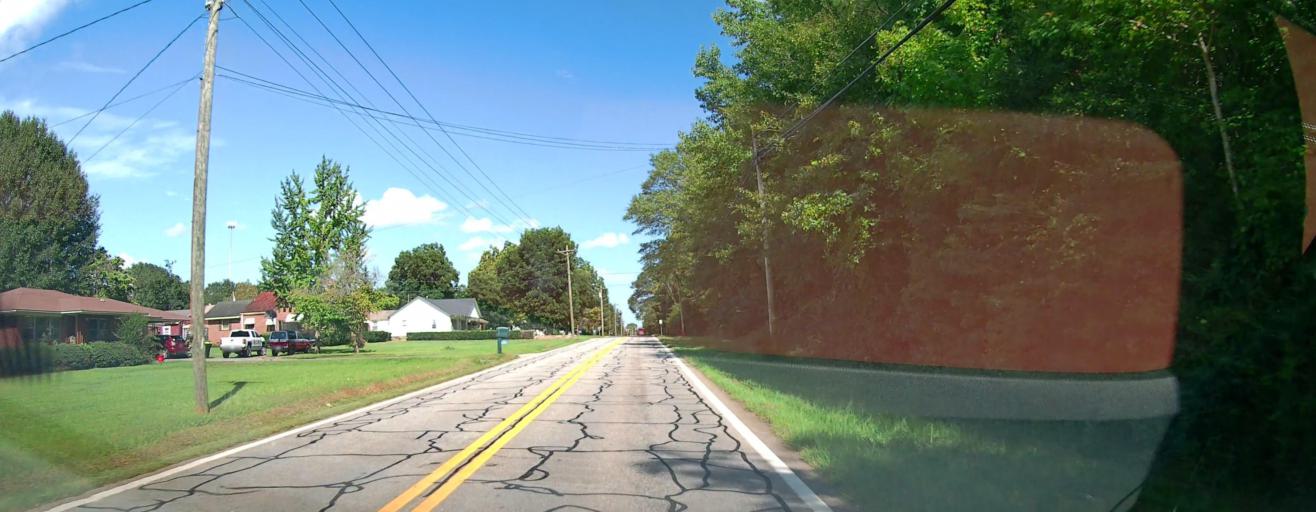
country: US
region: Georgia
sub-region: Upson County
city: Hannahs Mill
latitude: 32.9349
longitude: -84.3421
